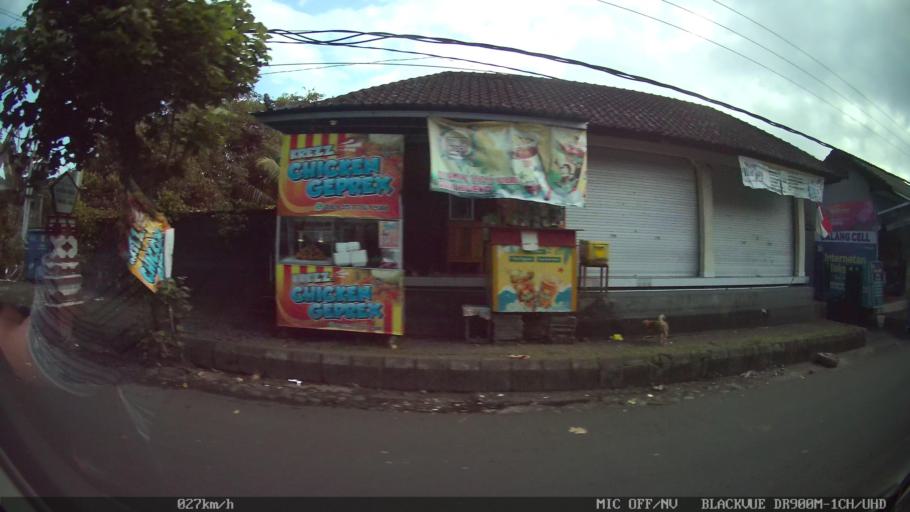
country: ID
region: Bali
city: Tabanan
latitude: -8.5420
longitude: 115.1235
